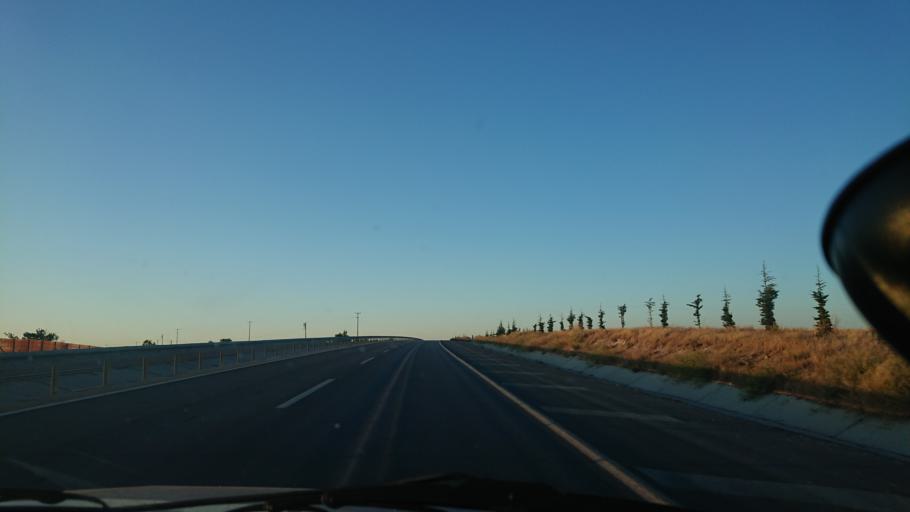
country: TR
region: Eskisehir
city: Mahmudiye
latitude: 39.5051
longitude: 30.9660
